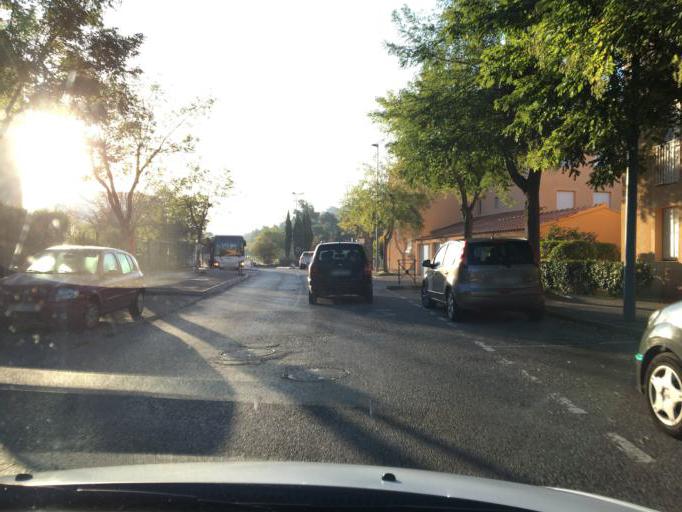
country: FR
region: Provence-Alpes-Cote d'Azur
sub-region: Departement des Bouches-du-Rhone
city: Aix-en-Provence
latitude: 43.5286
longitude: 5.4106
